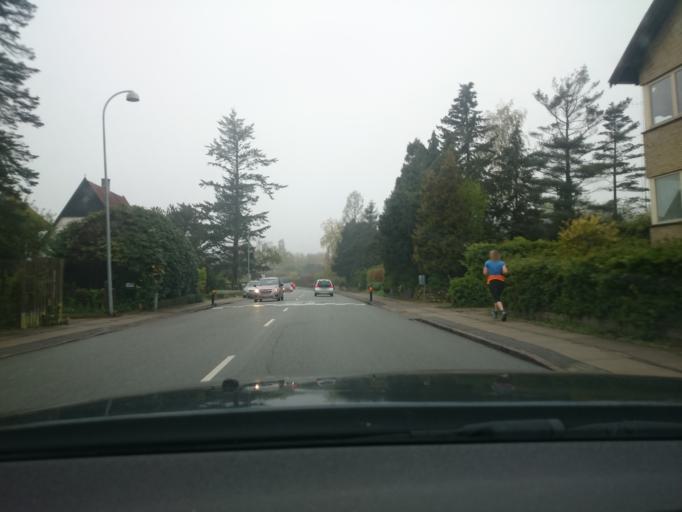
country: DK
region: Capital Region
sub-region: Gladsaxe Municipality
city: Buddinge
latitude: 55.7500
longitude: 12.4999
